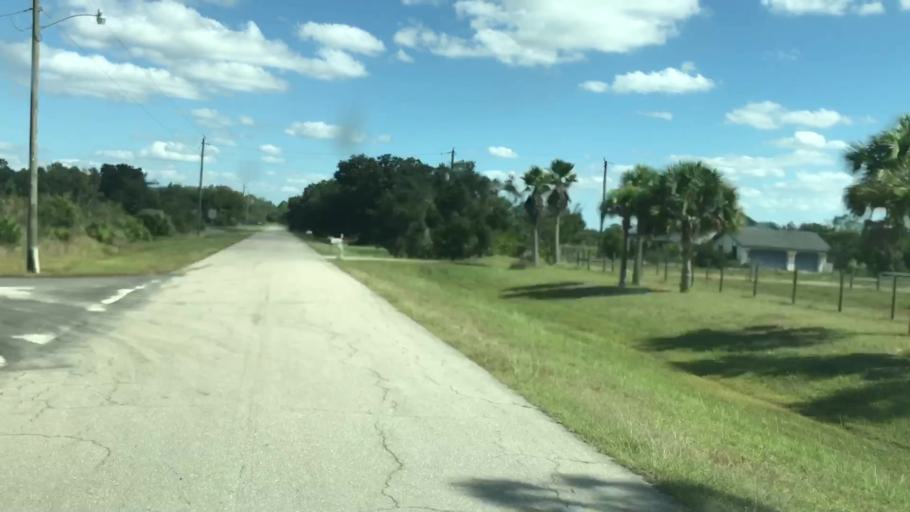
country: US
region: Florida
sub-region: Lee County
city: Alva
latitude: 26.6840
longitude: -81.5710
